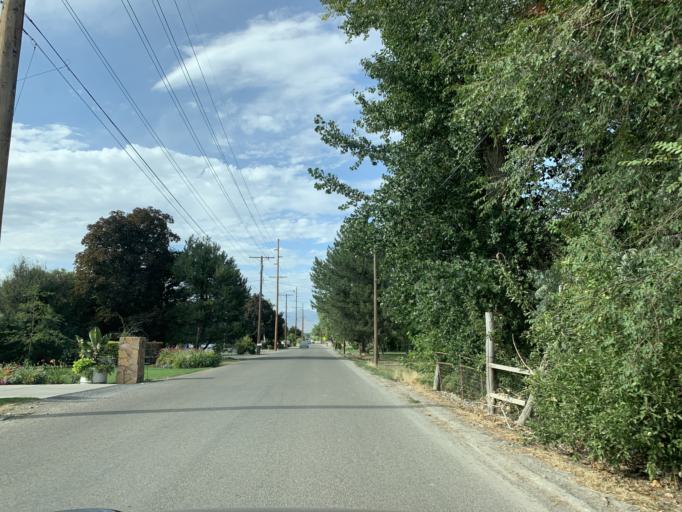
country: US
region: Utah
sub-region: Utah County
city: Provo
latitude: 40.2231
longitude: -111.6873
